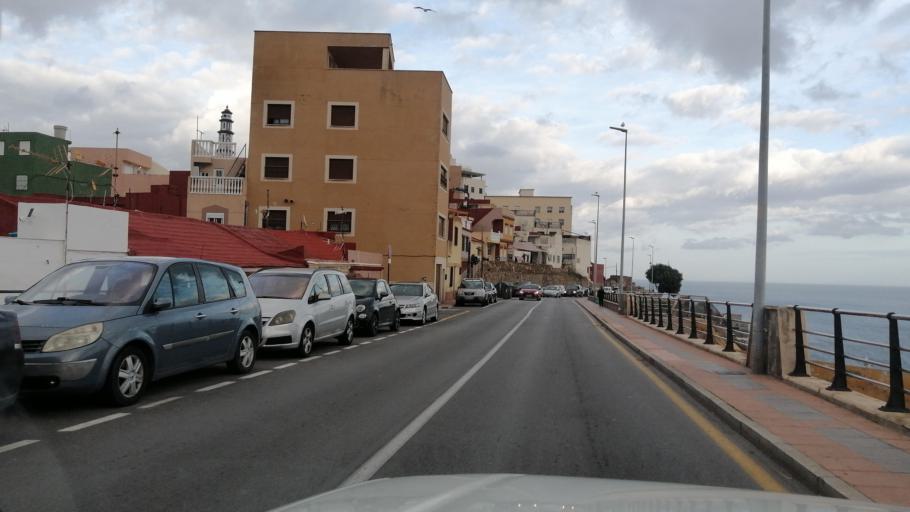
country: ES
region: Ceuta
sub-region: Ceuta
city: Ceuta
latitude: 35.8867
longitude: -5.3029
